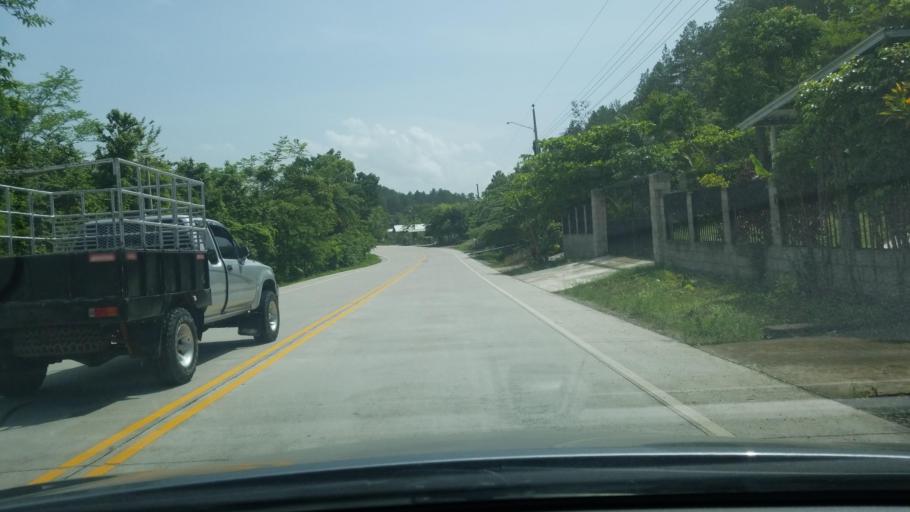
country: HN
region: Copan
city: Florida
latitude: 15.0043
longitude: -88.8366
